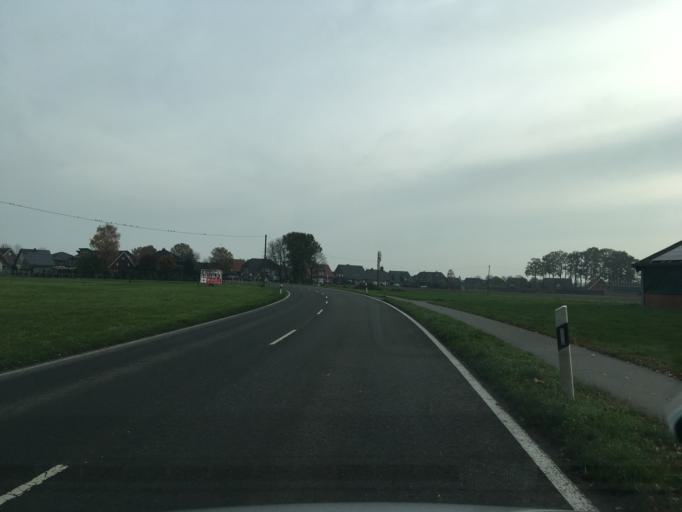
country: DE
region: North Rhine-Westphalia
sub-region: Regierungsbezirk Munster
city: Sudlohn
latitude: 51.9503
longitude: 6.8578
